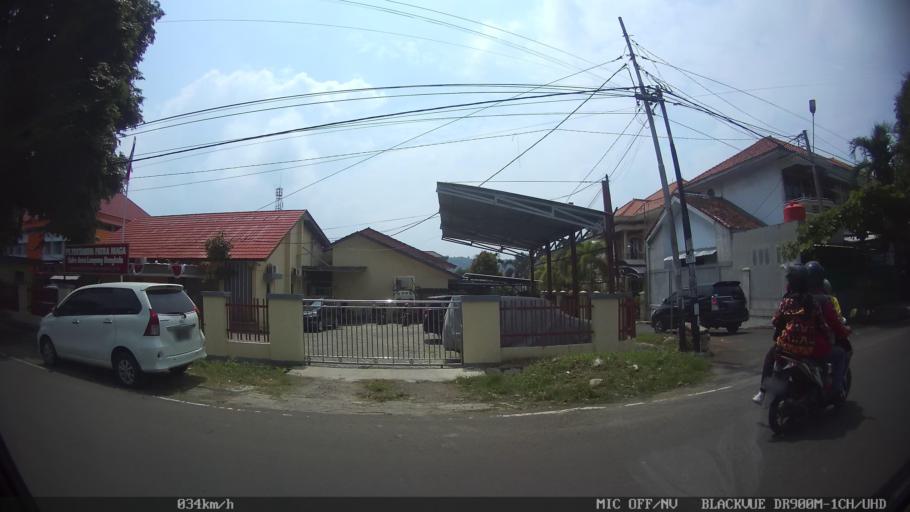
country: ID
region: Lampung
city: Bandarlampung
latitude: -5.4255
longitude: 105.2719
